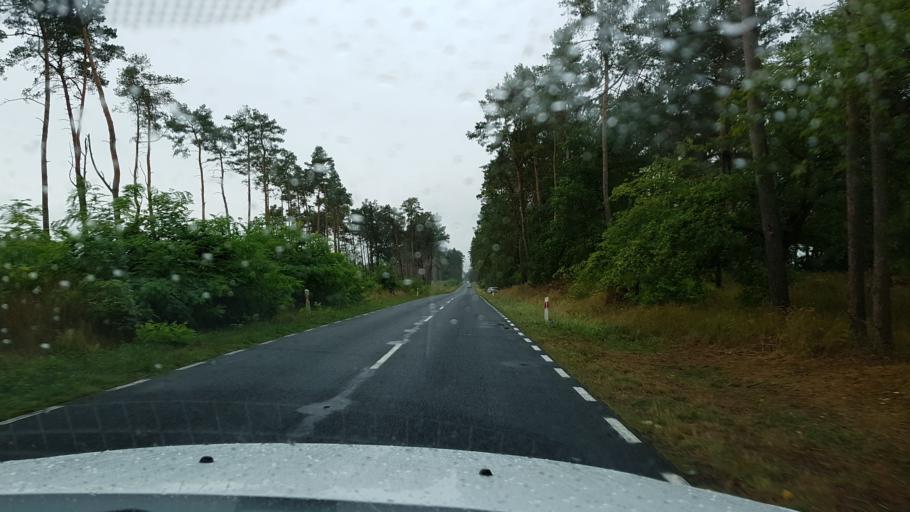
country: DE
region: Brandenburg
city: Schwedt (Oder)
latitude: 53.0472
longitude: 14.3407
